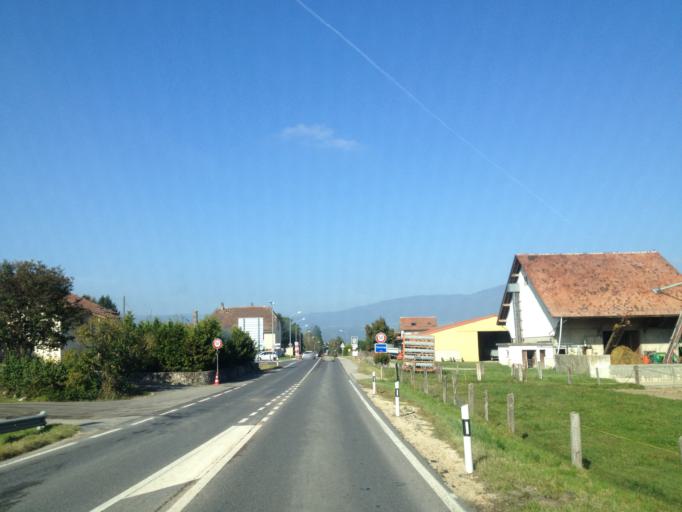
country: CH
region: Vaud
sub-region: Jura-Nord vaudois District
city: Chavornay
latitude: 46.7068
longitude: 6.5779
